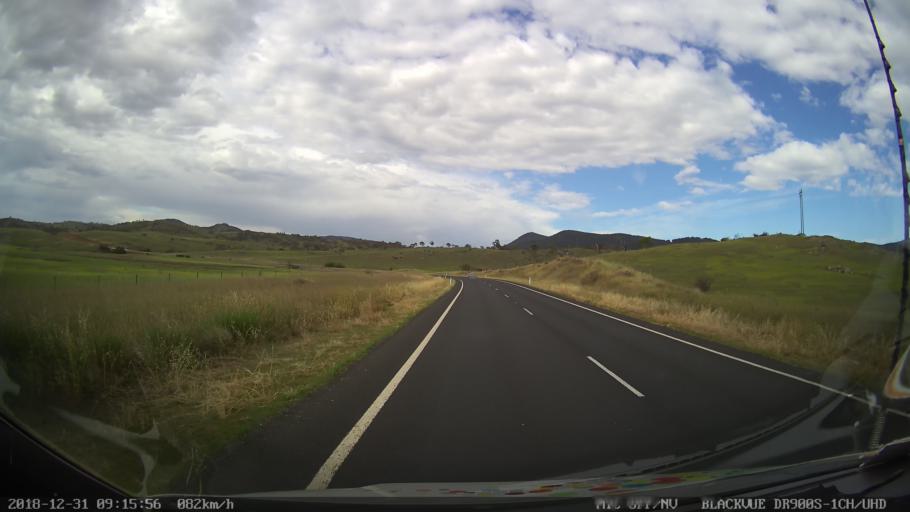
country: AU
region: New South Wales
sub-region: Snowy River
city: Jindabyne
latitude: -36.3908
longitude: 148.5961
